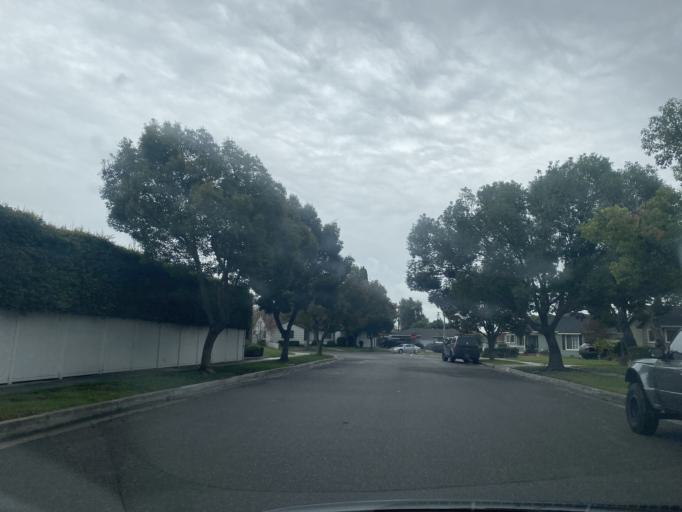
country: US
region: California
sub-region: Orange County
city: Fullerton
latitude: 33.8796
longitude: -117.9016
